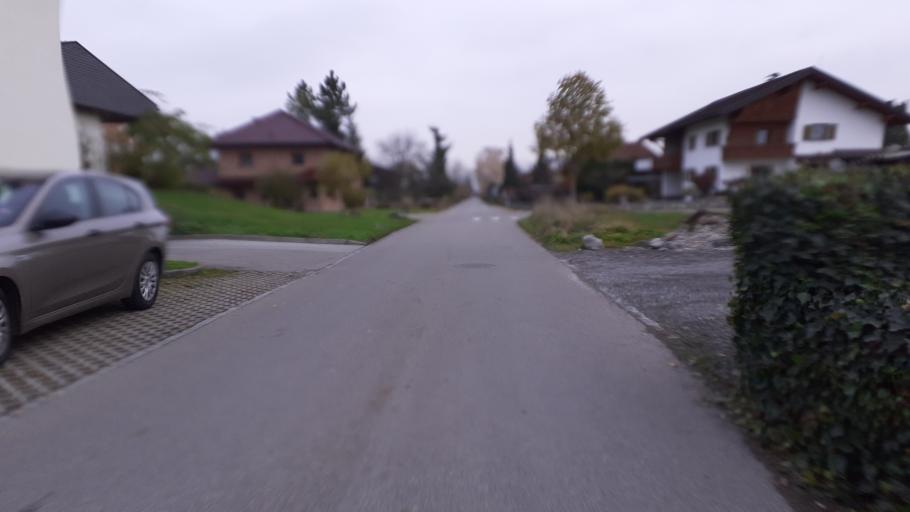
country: AT
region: Vorarlberg
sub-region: Politischer Bezirk Feldkirch
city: Nofels
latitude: 47.2605
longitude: 9.5881
